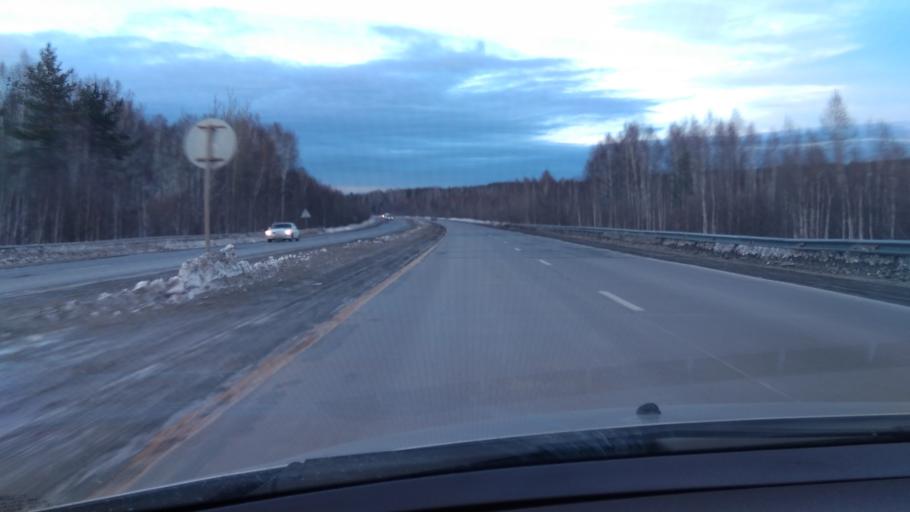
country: RU
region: Sverdlovsk
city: Shchelkun
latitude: 56.3195
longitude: 60.8699
